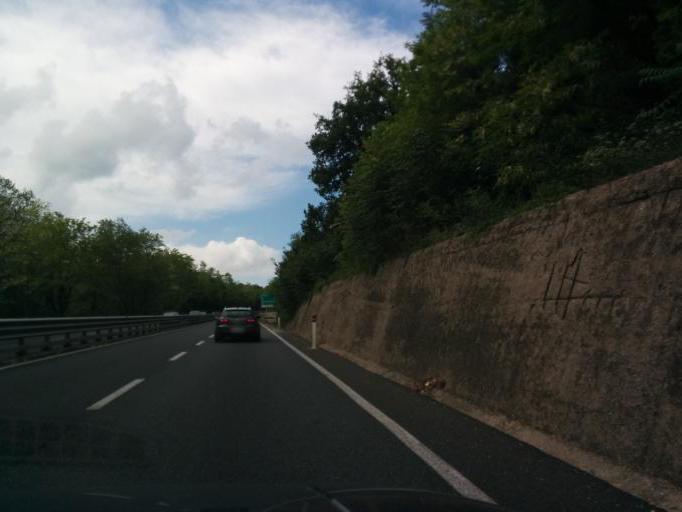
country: IT
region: Tuscany
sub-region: Province of Florence
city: Sambuca
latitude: 43.5605
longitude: 11.2127
